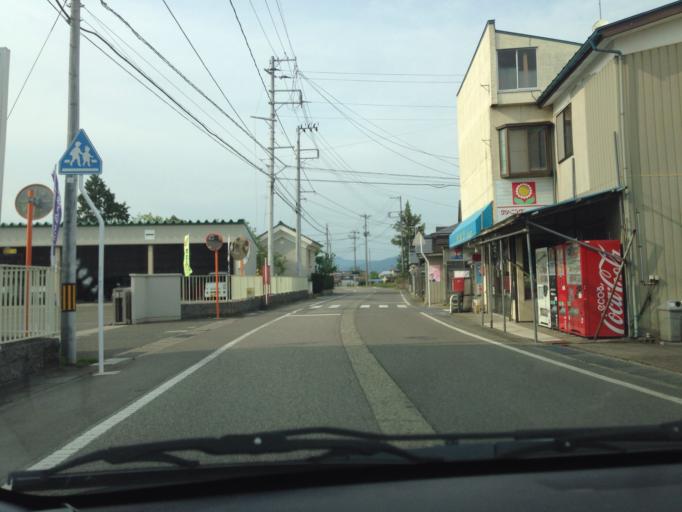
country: JP
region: Fukushima
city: Kitakata
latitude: 37.4593
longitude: 139.8941
